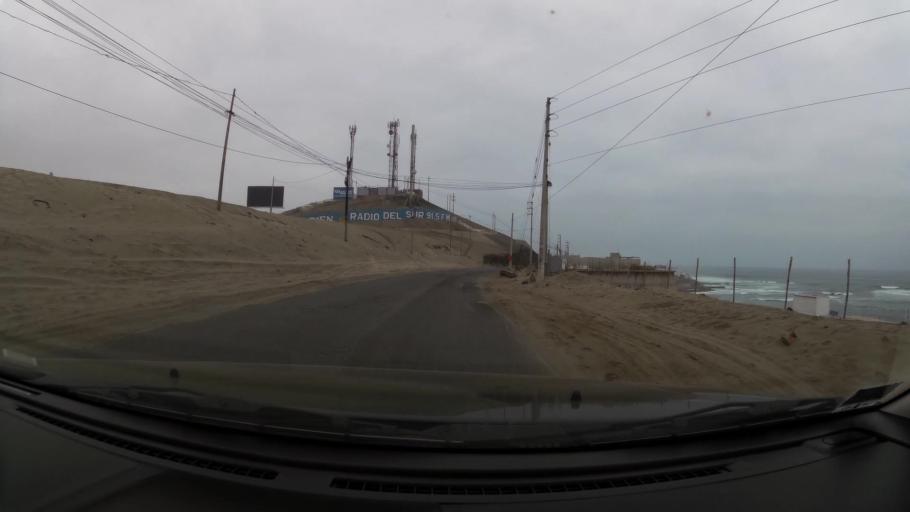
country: PE
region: Lima
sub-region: Lima
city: Punta Hermosa
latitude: -12.3406
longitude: -76.8160
